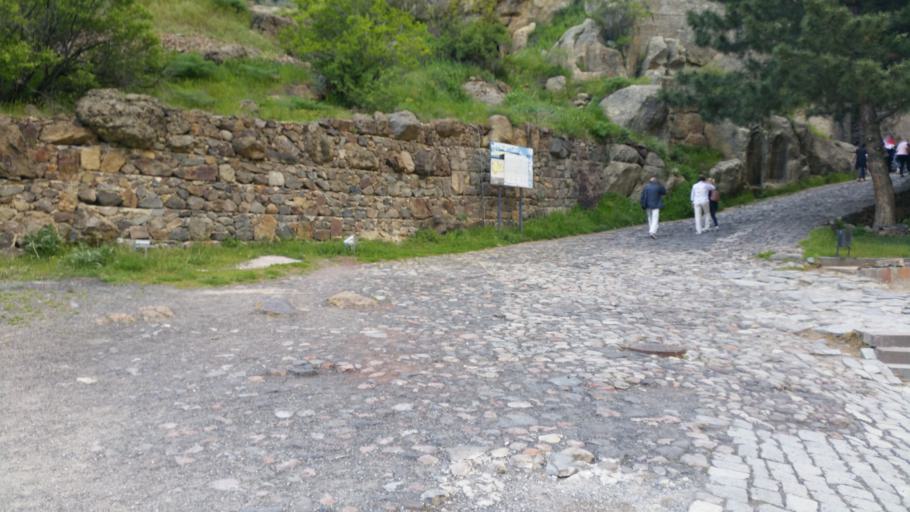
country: AM
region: Kotayk'i Marz
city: Goght'
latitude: 40.1399
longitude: 44.8177
